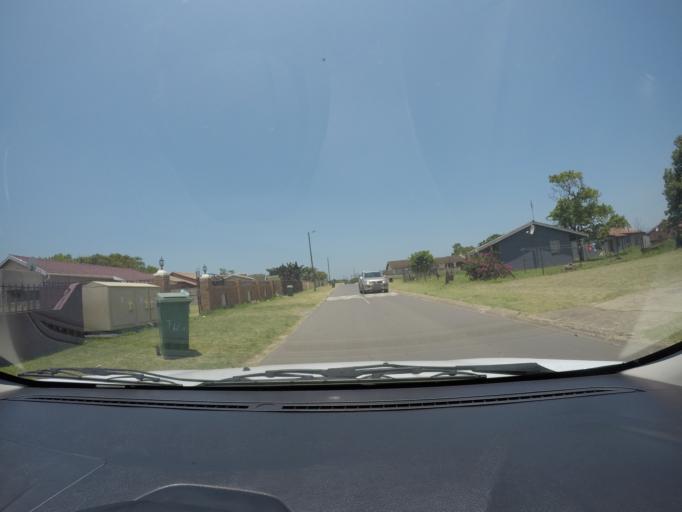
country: ZA
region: KwaZulu-Natal
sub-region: uThungulu District Municipality
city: eSikhawini
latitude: -28.8845
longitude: 31.8985
